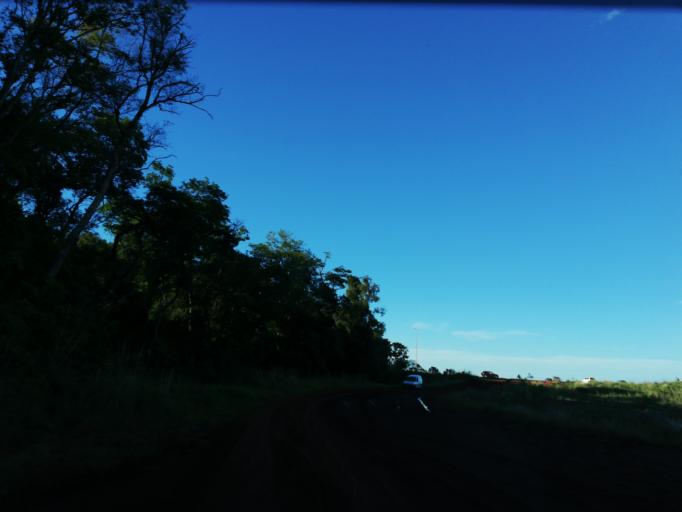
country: AR
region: Misiones
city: Garupa
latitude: -27.4594
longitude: -55.8132
